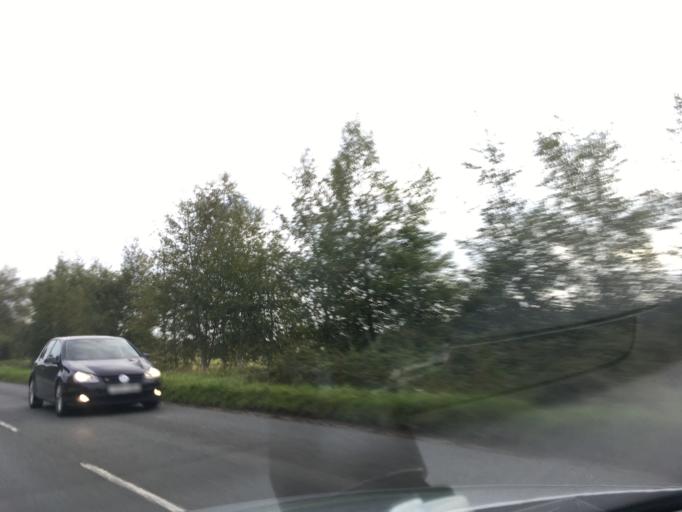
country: GB
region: England
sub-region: Oxfordshire
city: Cowley
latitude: 51.7753
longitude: -1.1890
